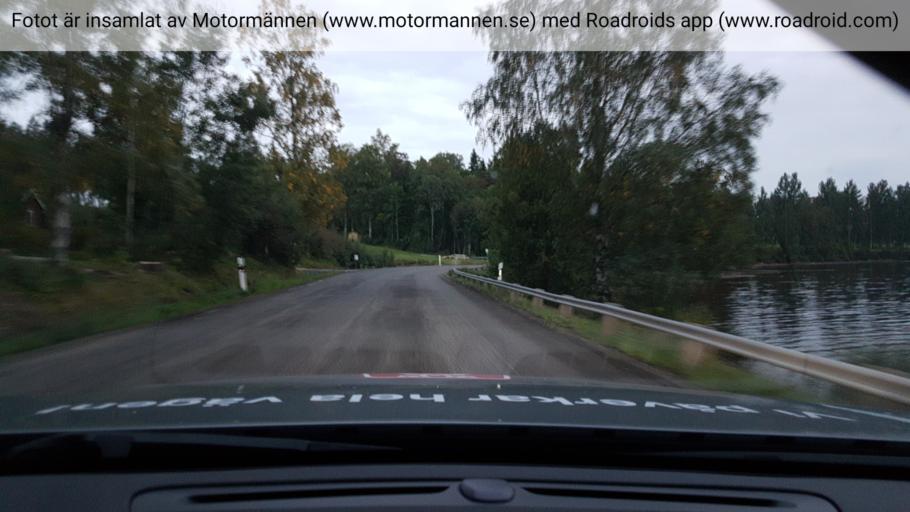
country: SE
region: OErebro
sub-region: Nora Kommun
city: As
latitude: 59.4810
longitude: 14.9225
